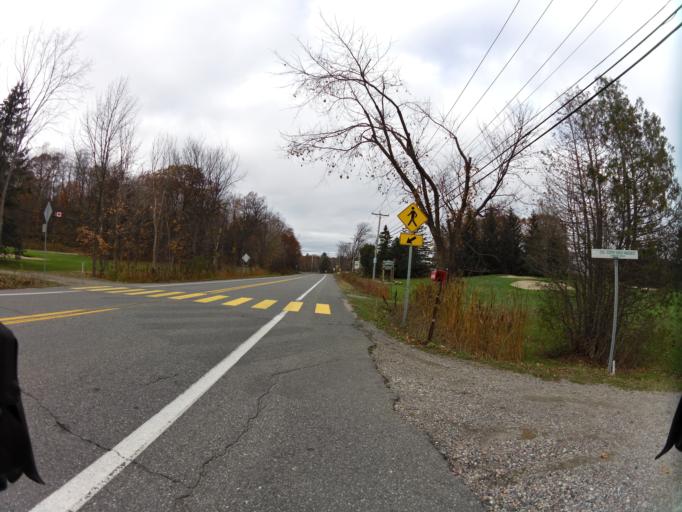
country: CA
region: Quebec
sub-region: Outaouais
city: Wakefield
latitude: 45.5531
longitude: -75.8277
